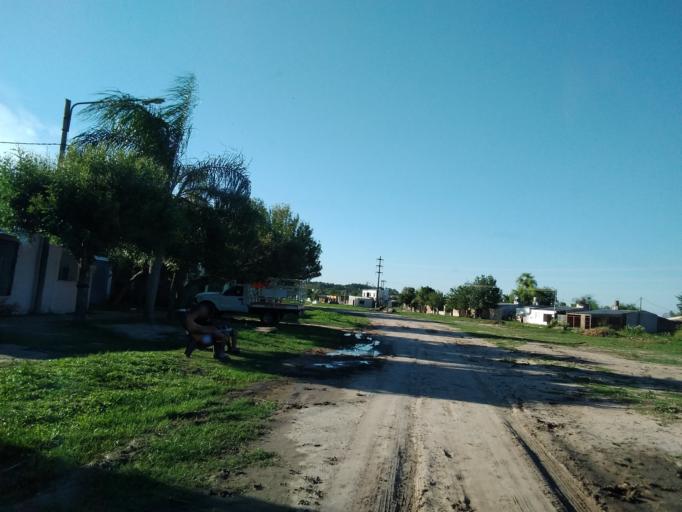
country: AR
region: Corrientes
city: Corrientes
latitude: -27.5078
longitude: -58.7780
